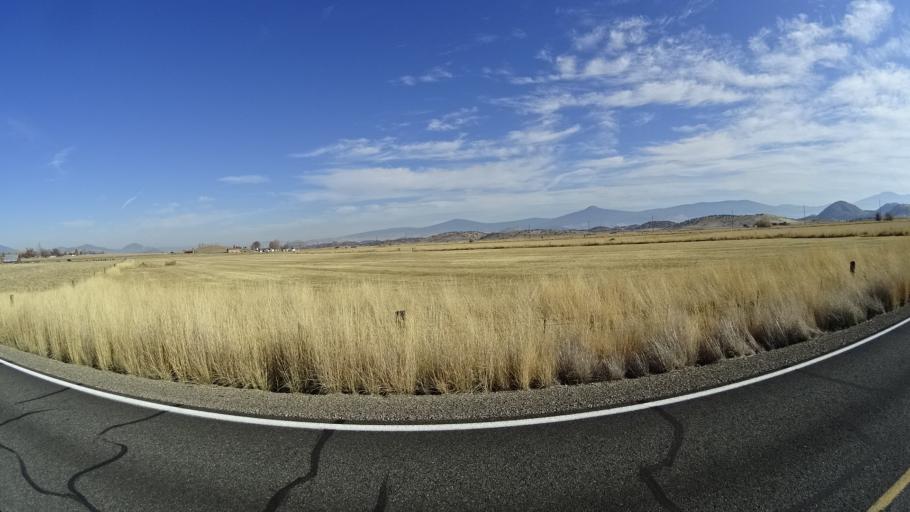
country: US
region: California
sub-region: Siskiyou County
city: Montague
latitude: 41.6068
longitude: -122.5279
